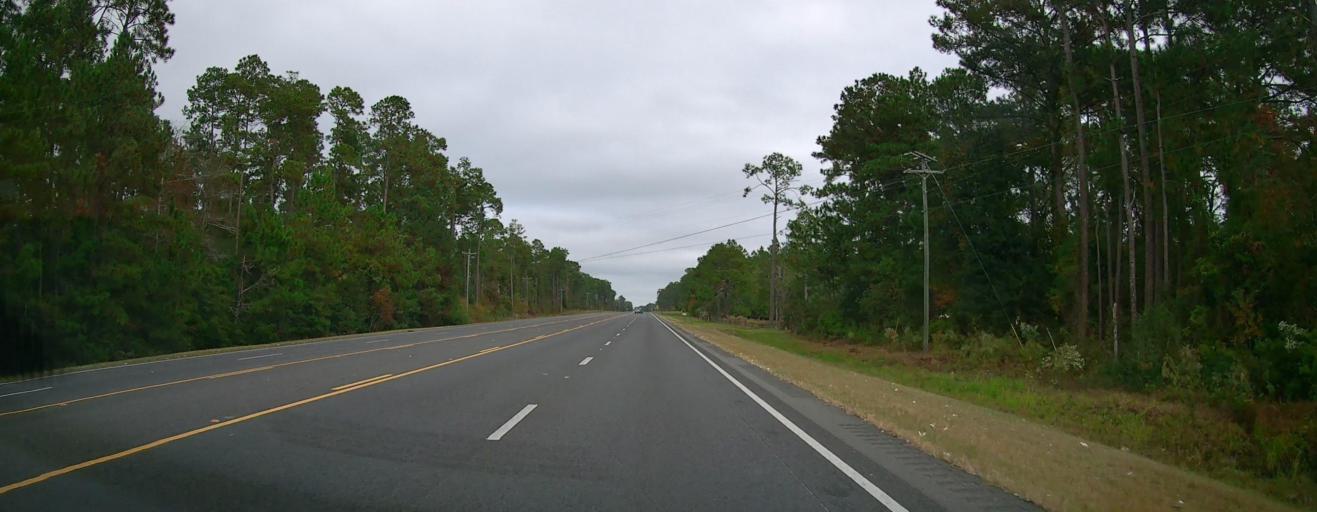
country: US
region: Georgia
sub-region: Colquitt County
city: Moultrie
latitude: 31.0836
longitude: -83.8152
